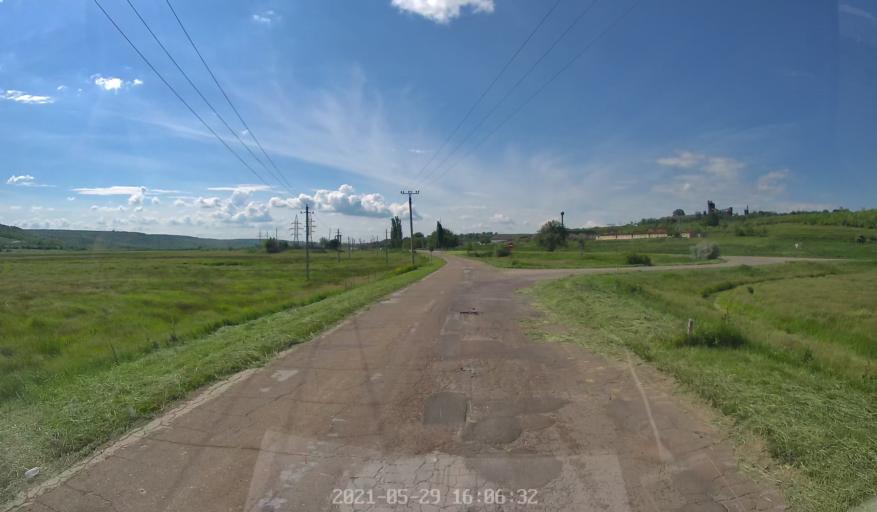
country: MD
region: Chisinau
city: Singera
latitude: 46.8147
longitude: 28.9067
